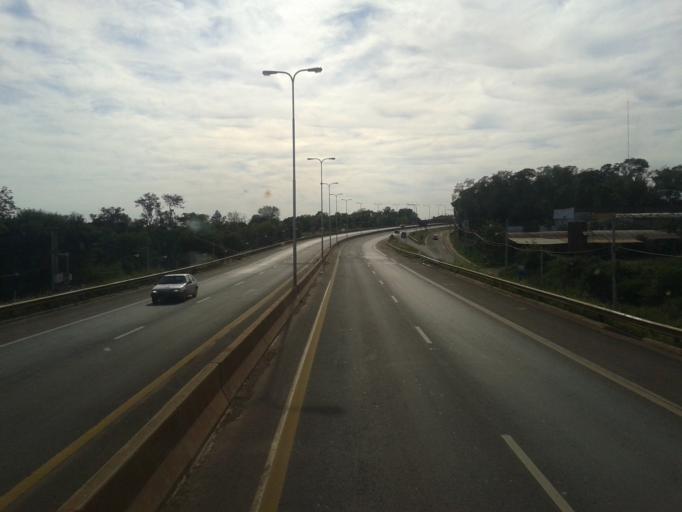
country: AR
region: Misiones
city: Garupa
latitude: -27.4596
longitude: -55.8289
